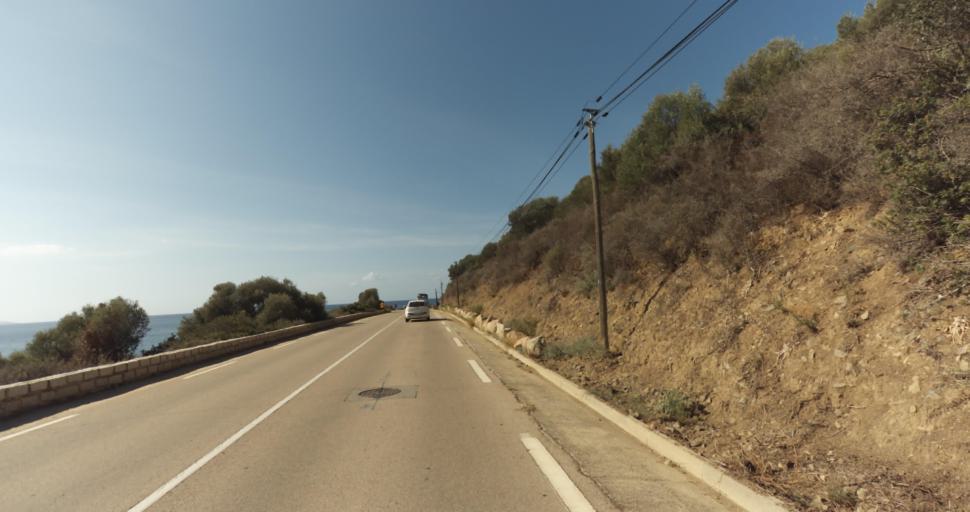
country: FR
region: Corsica
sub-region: Departement de la Corse-du-Sud
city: Ajaccio
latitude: 41.9044
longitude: 8.6263
